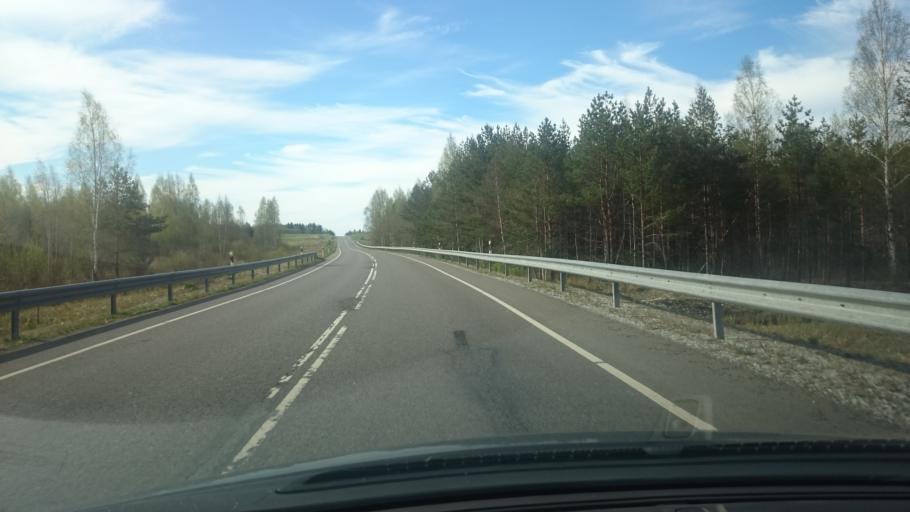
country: EE
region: Ida-Virumaa
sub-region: Johvi vald
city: Johvi
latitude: 59.1898
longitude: 27.5595
